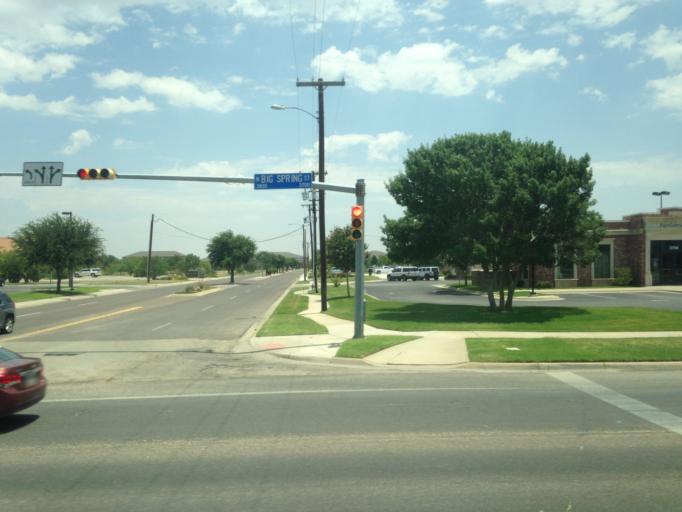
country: US
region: Texas
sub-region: Midland County
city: Midland
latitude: 32.0352
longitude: -102.0854
